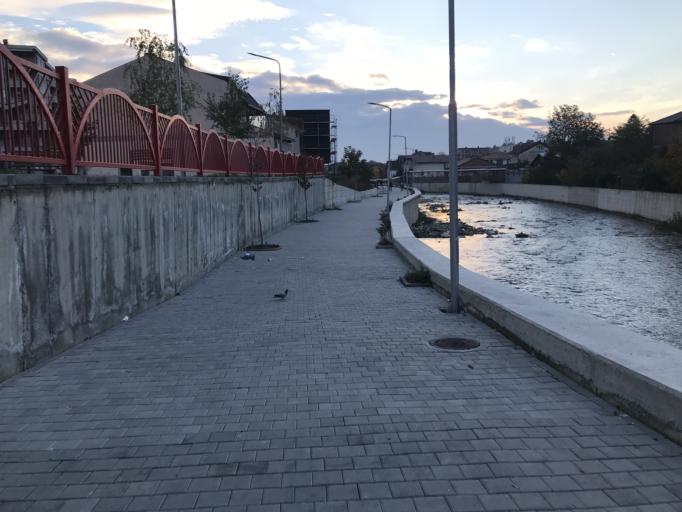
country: XK
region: Pec
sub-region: Komuna e Pejes
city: Peje
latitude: 42.6594
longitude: 20.2795
